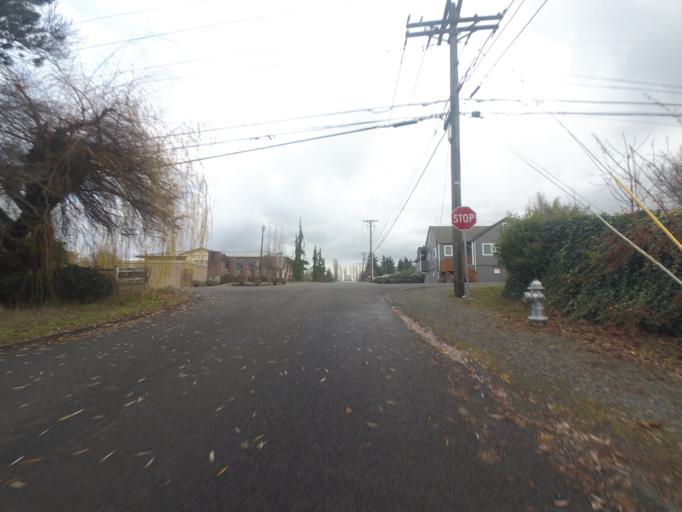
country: US
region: Washington
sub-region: Pierce County
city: University Place
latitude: 47.2345
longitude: -122.5393
